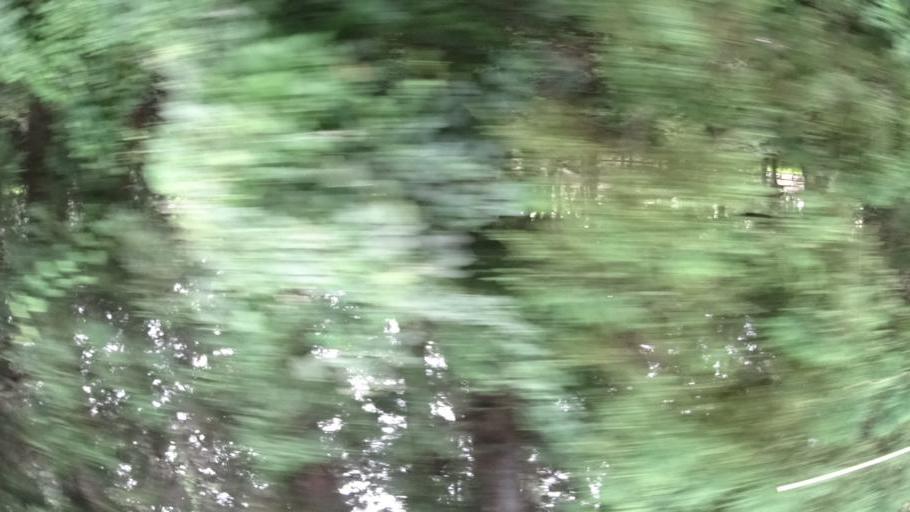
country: JP
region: Tochigi
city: Imaichi
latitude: 36.7174
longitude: 139.6934
